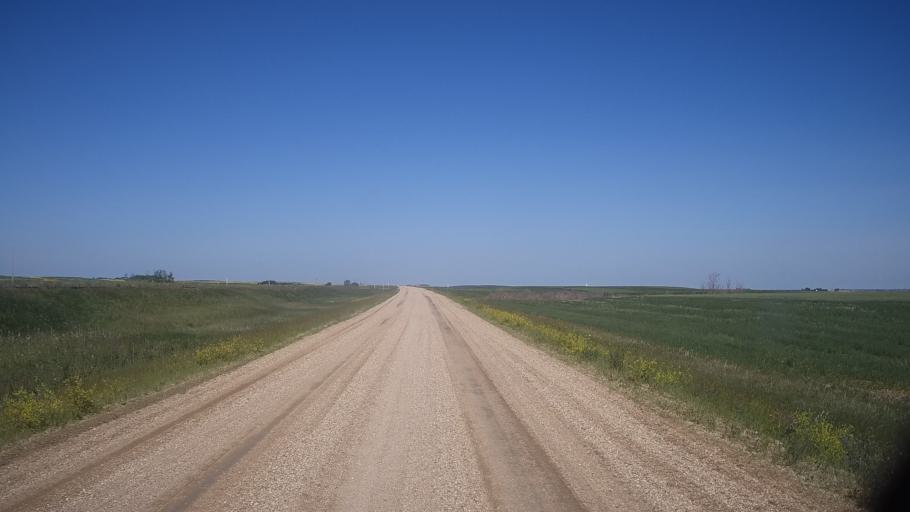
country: CA
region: Saskatchewan
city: Watrous
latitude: 51.8457
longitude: -105.9208
